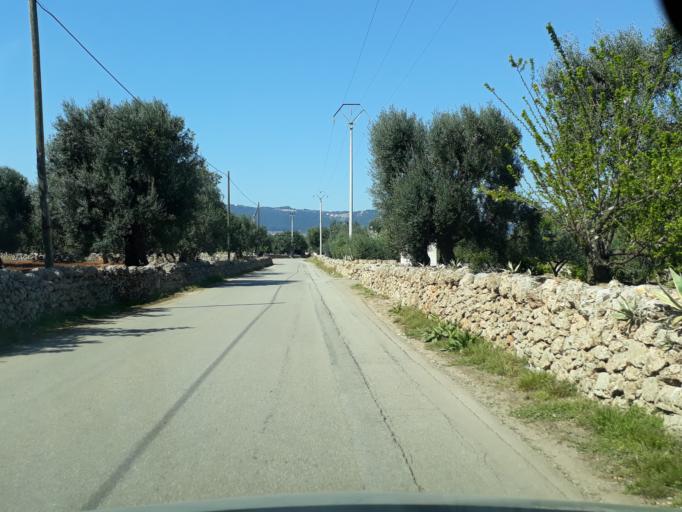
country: IT
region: Apulia
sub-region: Provincia di Brindisi
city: Fasano
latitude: 40.8352
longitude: 17.3750
